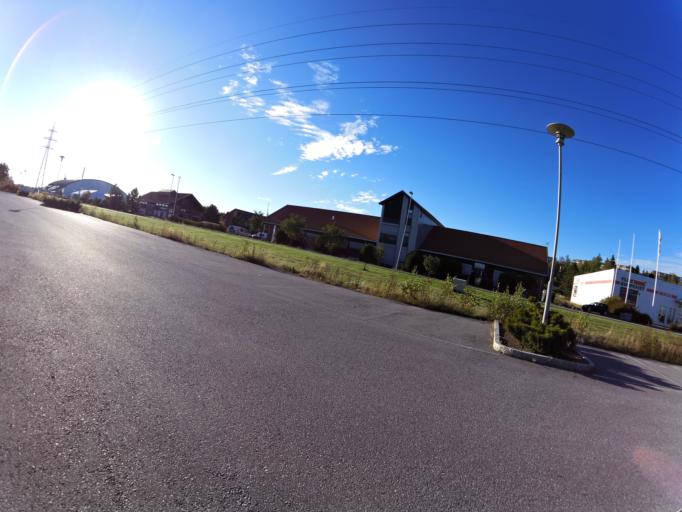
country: NO
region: Ostfold
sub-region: Fredrikstad
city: Fredrikstad
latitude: 59.2543
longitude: 10.9998
